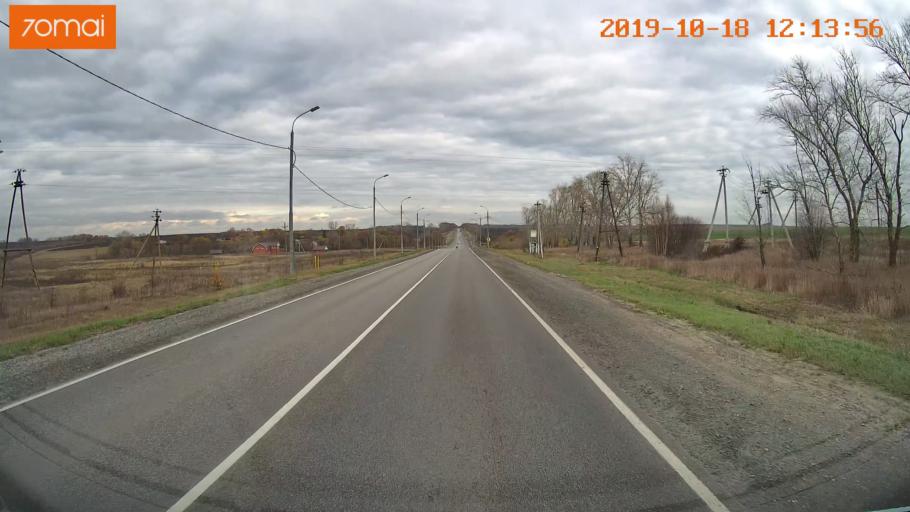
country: RU
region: Rjazan
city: Zakharovo
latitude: 54.4249
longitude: 39.3752
